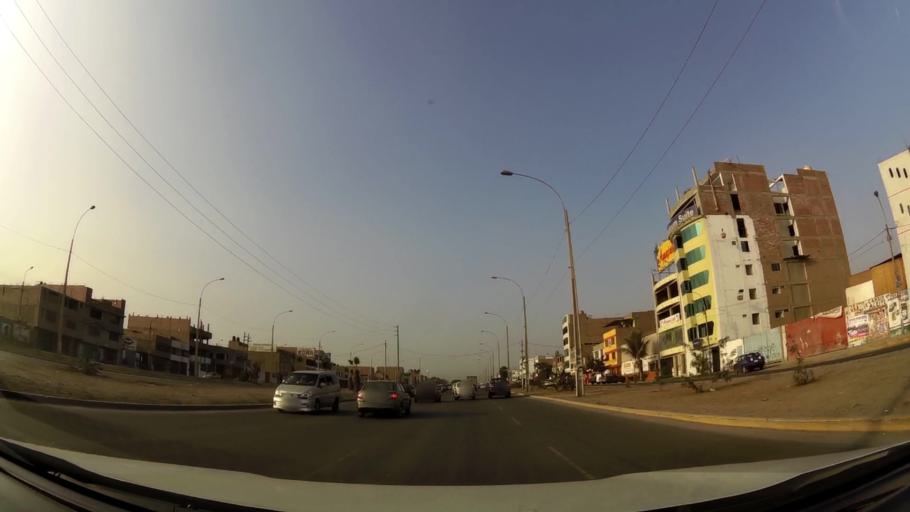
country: PE
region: Lima
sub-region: Lima
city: Independencia
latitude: -11.9808
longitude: -77.0960
